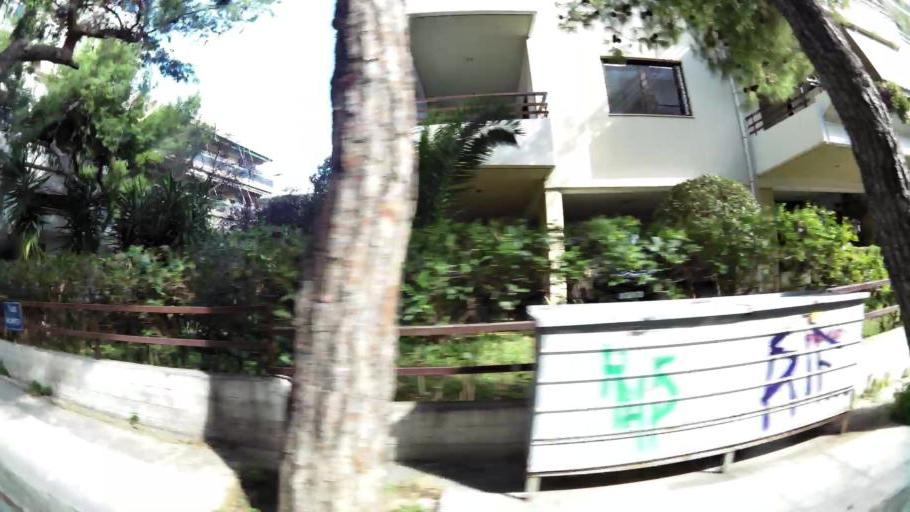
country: GR
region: Attica
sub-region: Nomarchia Athinas
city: Neo Psychiko
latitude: 38.0048
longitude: 23.7815
